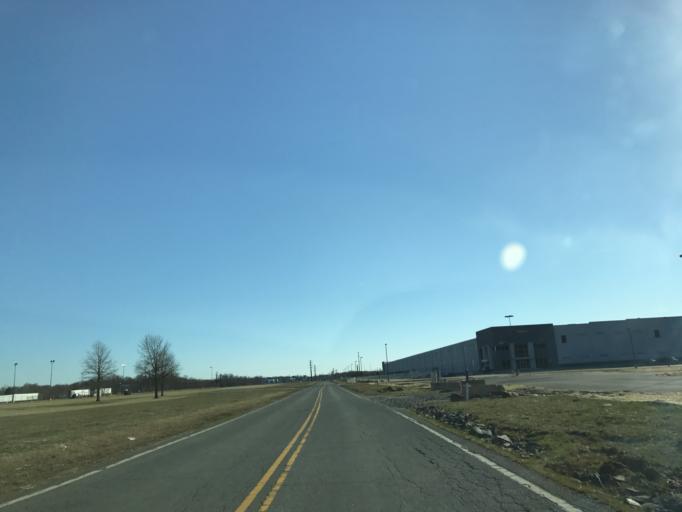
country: US
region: Maryland
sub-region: Harford County
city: Perryman
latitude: 39.4525
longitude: -76.2125
